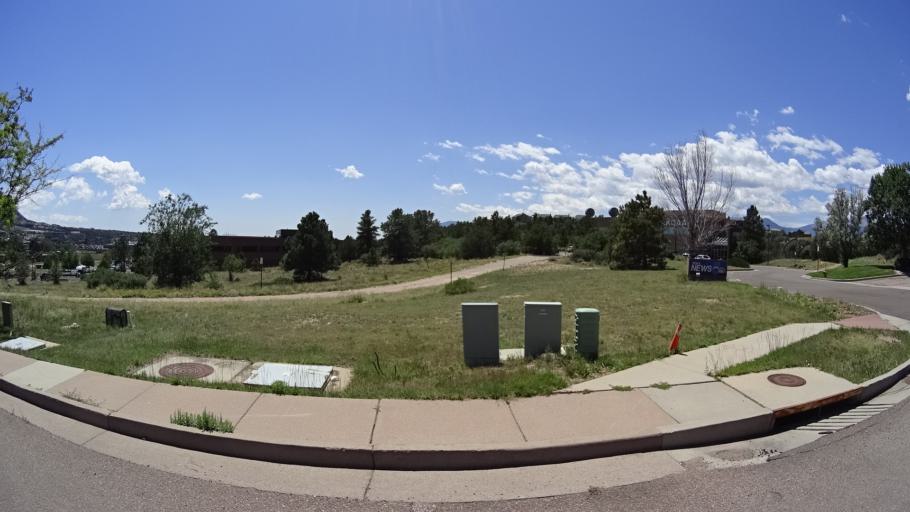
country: US
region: Colorado
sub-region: El Paso County
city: Colorado Springs
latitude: 38.9116
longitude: -104.8275
